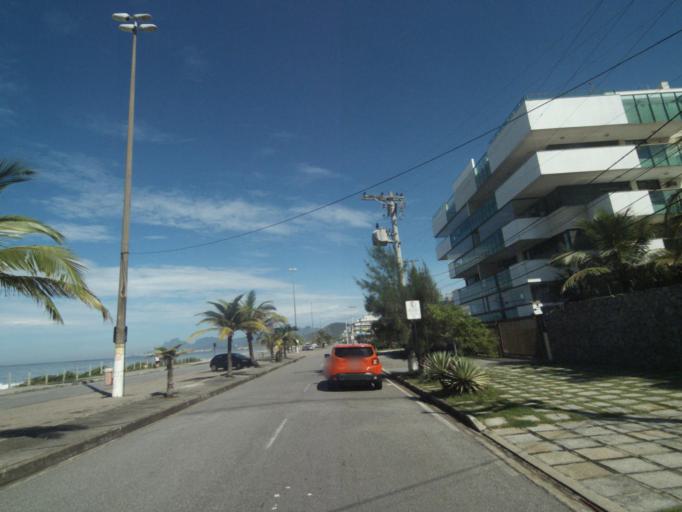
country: BR
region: Rio de Janeiro
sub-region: Niteroi
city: Niteroi
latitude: -22.9551
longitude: -43.0781
